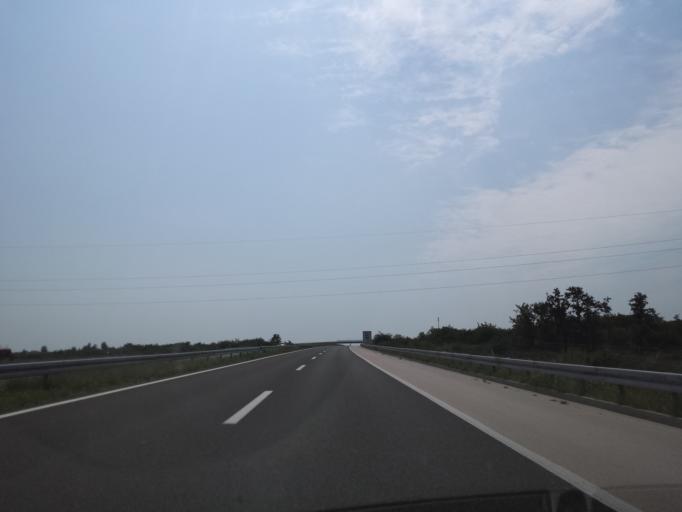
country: HR
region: Zadarska
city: Policnik
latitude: 44.1477
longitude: 15.4208
